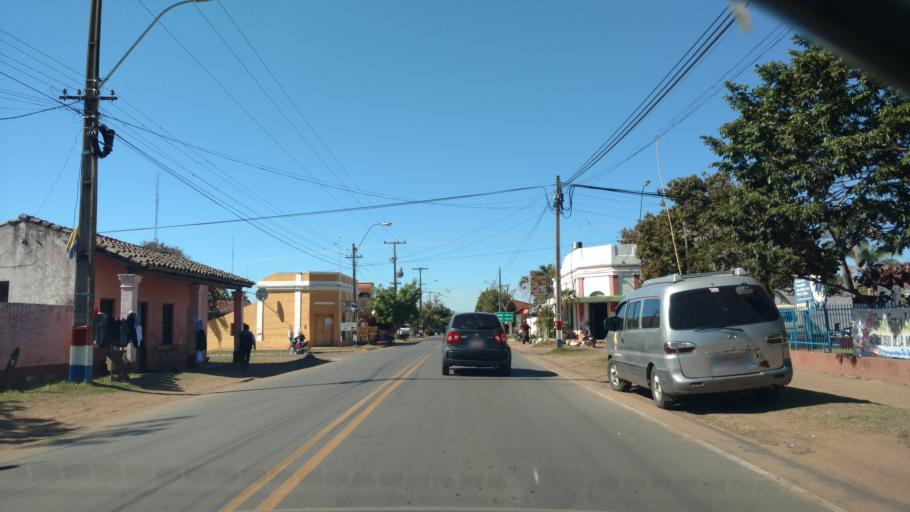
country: PY
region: Paraguari
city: Pirayu
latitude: -25.4846
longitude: -57.2371
